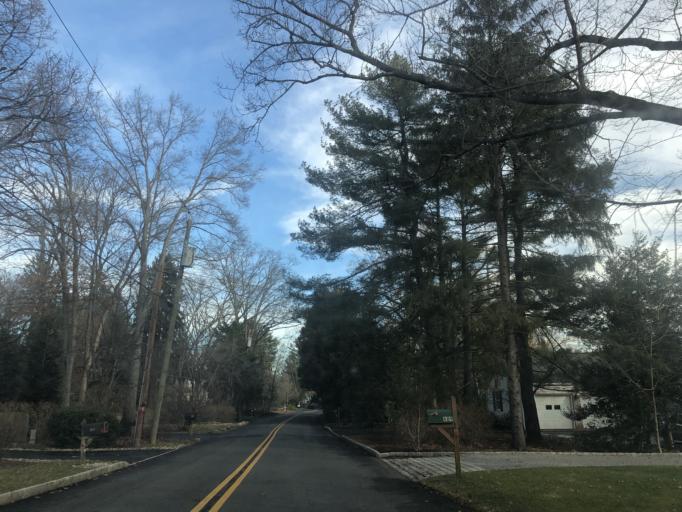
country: US
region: New Jersey
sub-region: Somerset County
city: Kingston
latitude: 40.3627
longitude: -74.6278
